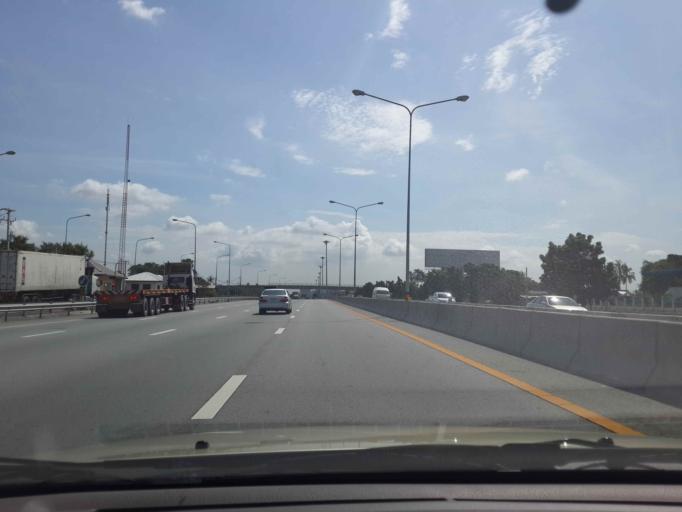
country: TH
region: Chon Buri
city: Chon Buri
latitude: 13.3209
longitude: 101.0122
